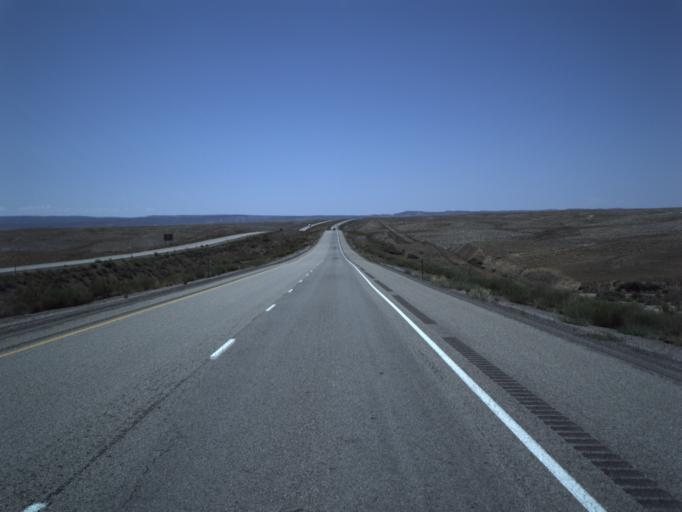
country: US
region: Colorado
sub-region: Mesa County
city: Loma
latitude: 39.0254
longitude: -109.2950
